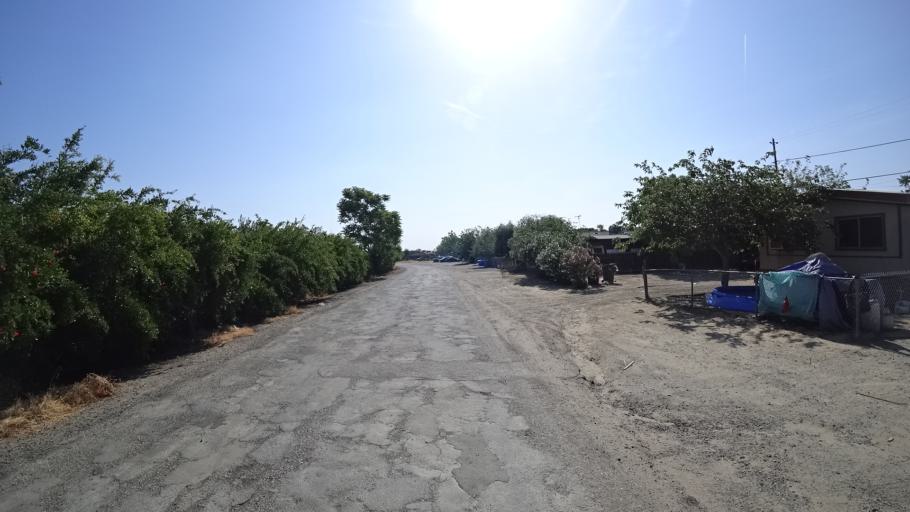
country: US
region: California
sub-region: Kings County
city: Kettleman City
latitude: 36.0116
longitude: -119.9644
